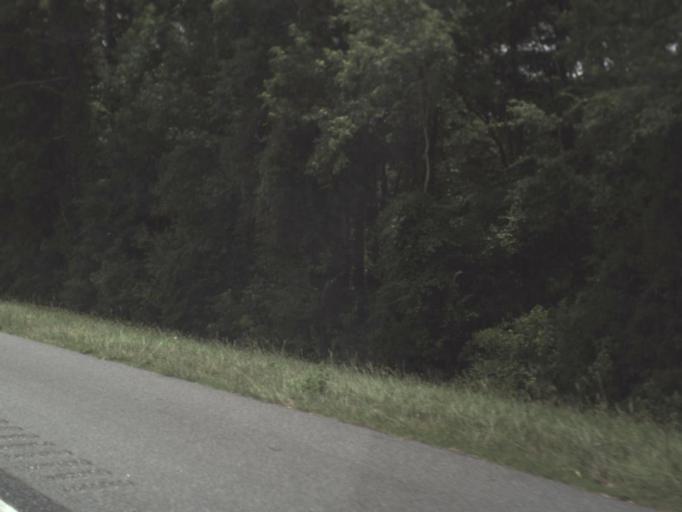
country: US
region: Florida
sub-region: Alachua County
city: High Springs
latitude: 29.9315
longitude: -82.5611
